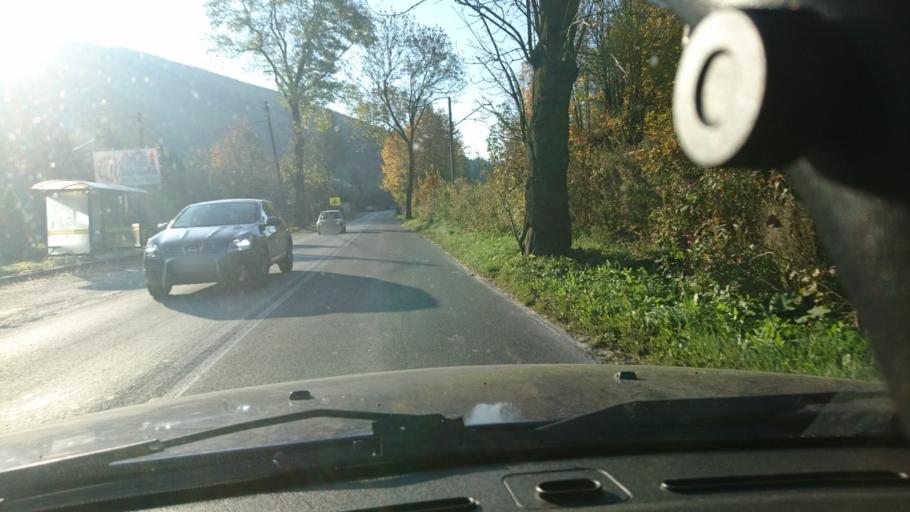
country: PL
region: Silesian Voivodeship
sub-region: Powiat cieszynski
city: Wisla
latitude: 49.6790
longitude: 18.8480
